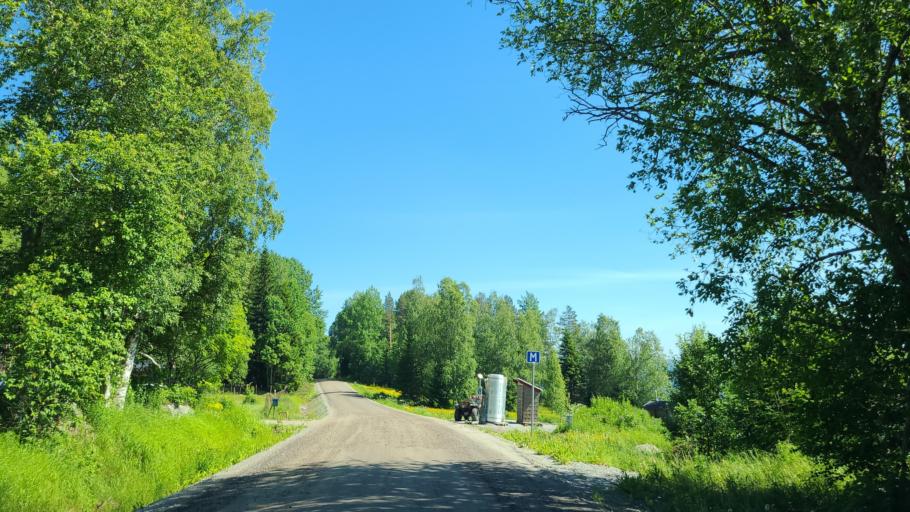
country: SE
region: Vaesterbotten
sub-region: Bjurholms Kommun
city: Bjurholm
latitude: 63.6766
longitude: 19.0119
